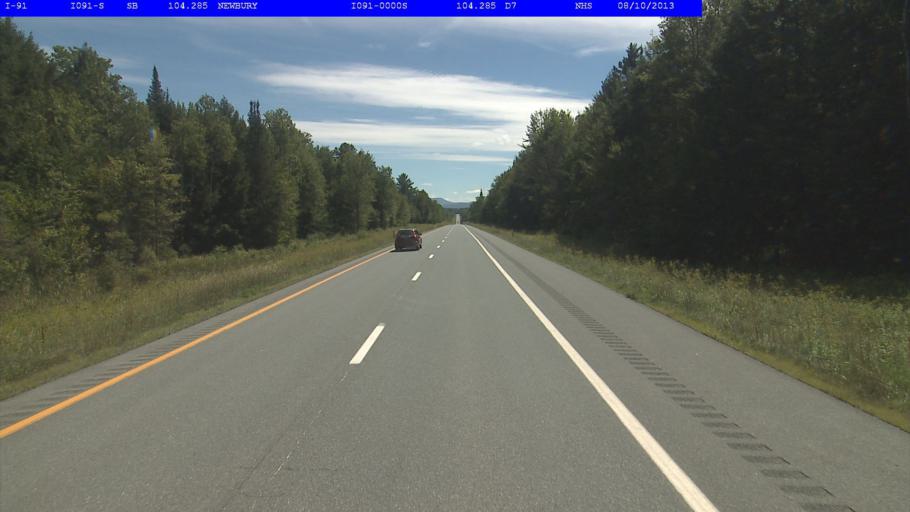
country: US
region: New Hampshire
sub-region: Grafton County
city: Haverhill
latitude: 44.0755
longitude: -72.1128
